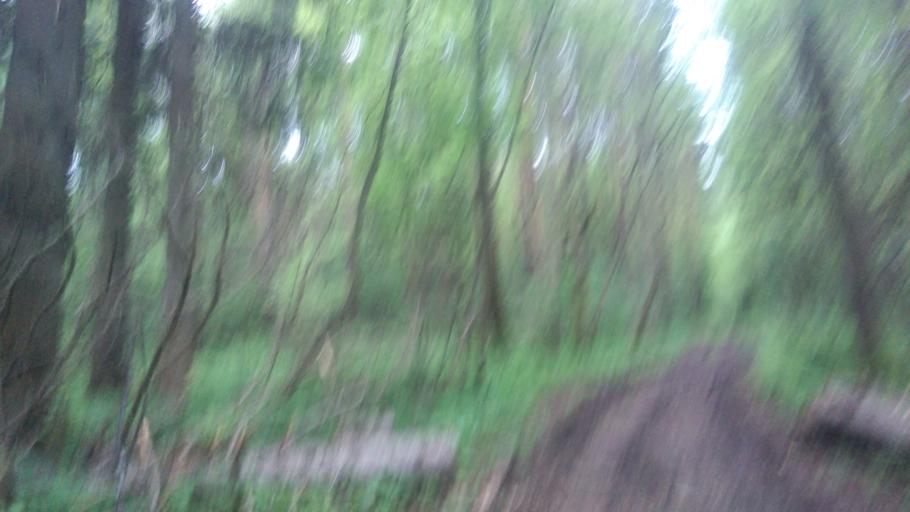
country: RU
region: Perm
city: Froly
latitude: 57.9626
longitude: 56.2988
